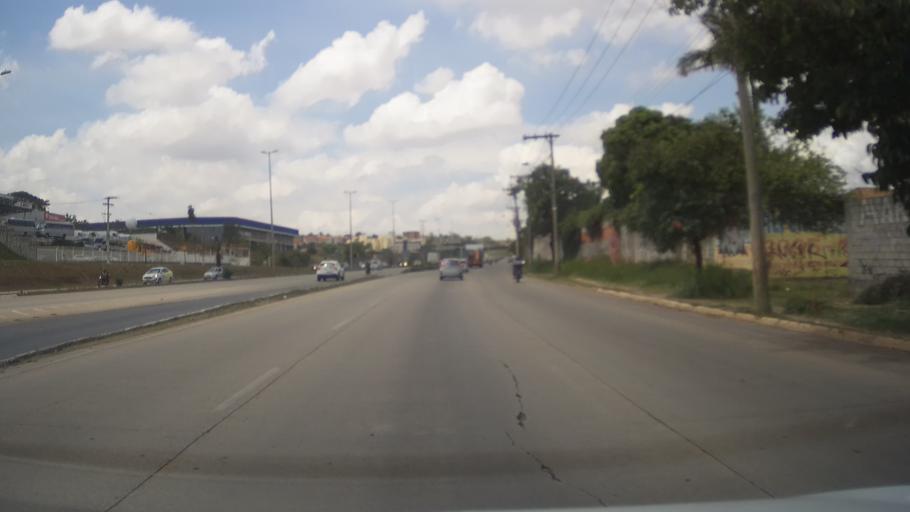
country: BR
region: Minas Gerais
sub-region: Contagem
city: Contagem
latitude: -19.9359
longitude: -44.0246
